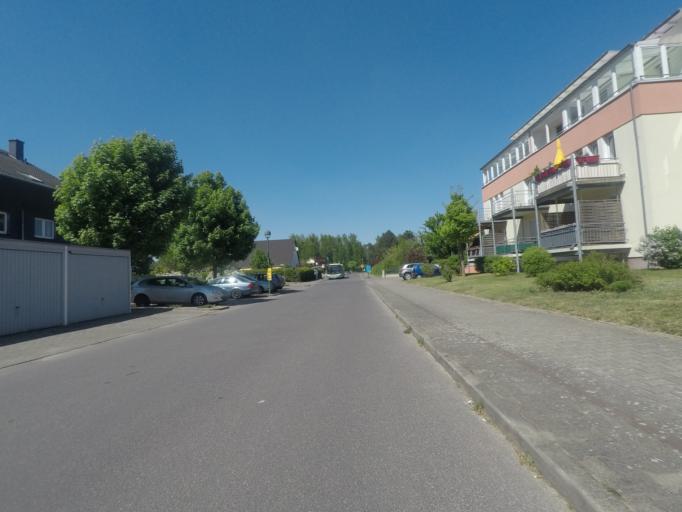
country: DE
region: Brandenburg
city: Melchow
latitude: 52.8511
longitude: 13.6948
